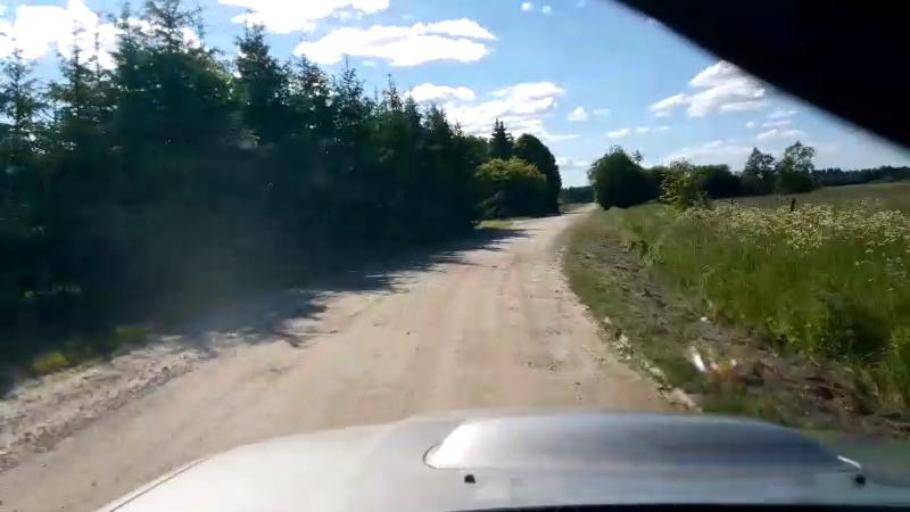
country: EE
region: Paernumaa
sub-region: Sauga vald
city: Sauga
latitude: 58.5093
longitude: 24.5506
